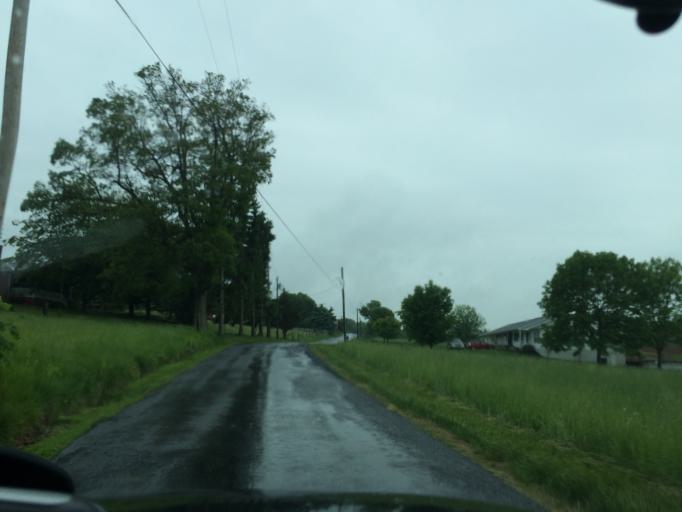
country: US
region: Maryland
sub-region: Washington County
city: Highfield-Cascade
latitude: 39.6962
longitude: -77.4785
